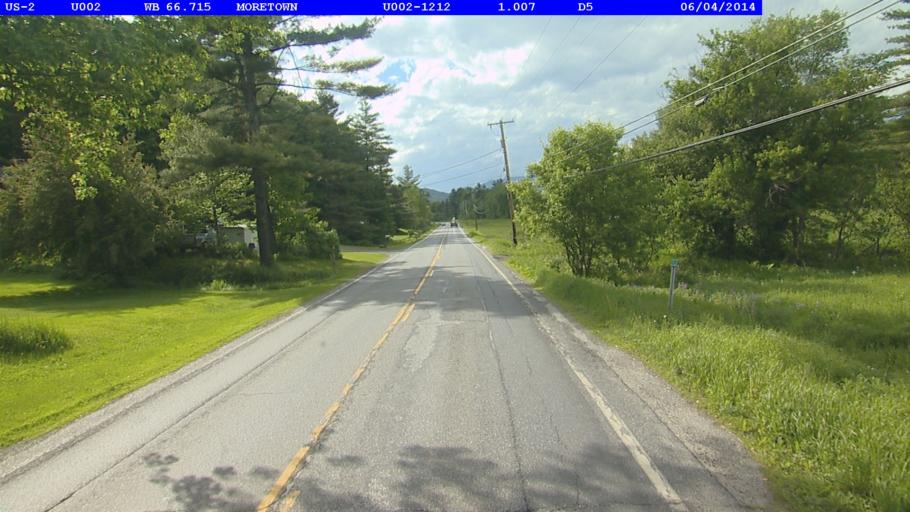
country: US
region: Vermont
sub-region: Washington County
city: Waterbury
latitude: 44.3188
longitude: -72.7303
